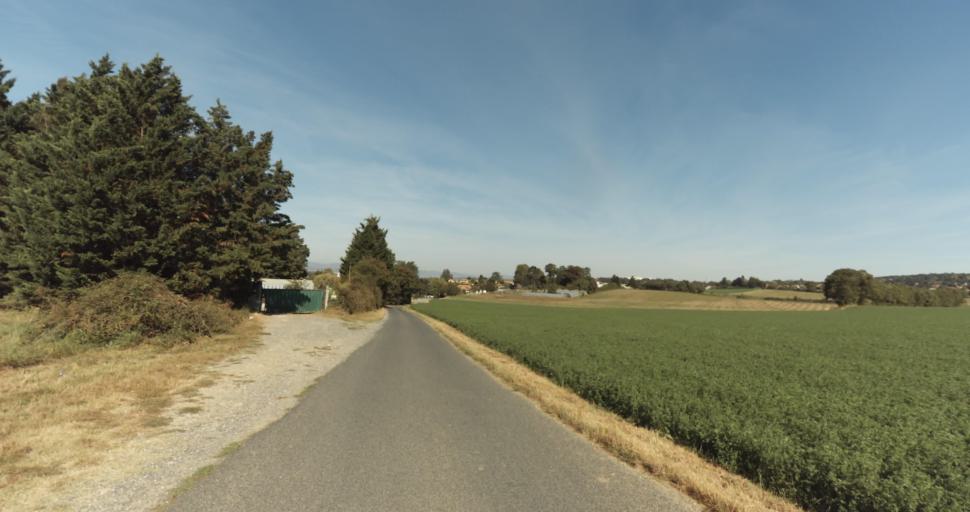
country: FR
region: Rhone-Alpes
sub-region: Departement du Rhone
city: Fleurieu-sur-Saone
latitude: 45.8665
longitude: 4.8504
